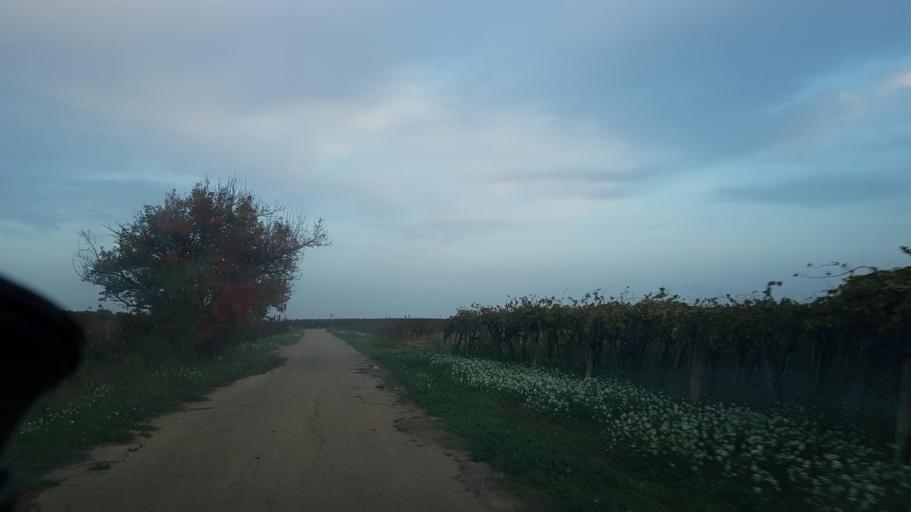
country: IT
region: Apulia
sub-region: Provincia di Brindisi
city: San Donaci
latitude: 40.4280
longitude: 17.9307
